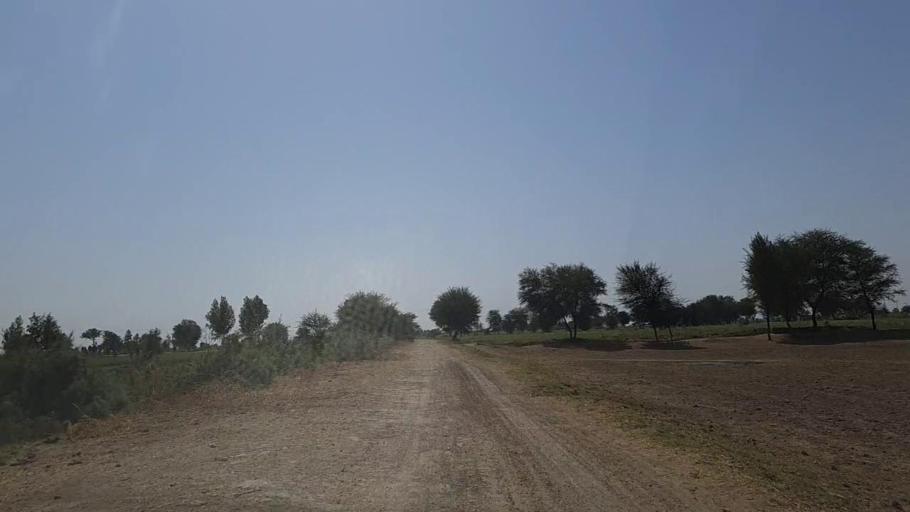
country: PK
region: Sindh
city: Samaro
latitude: 25.2168
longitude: 69.4053
